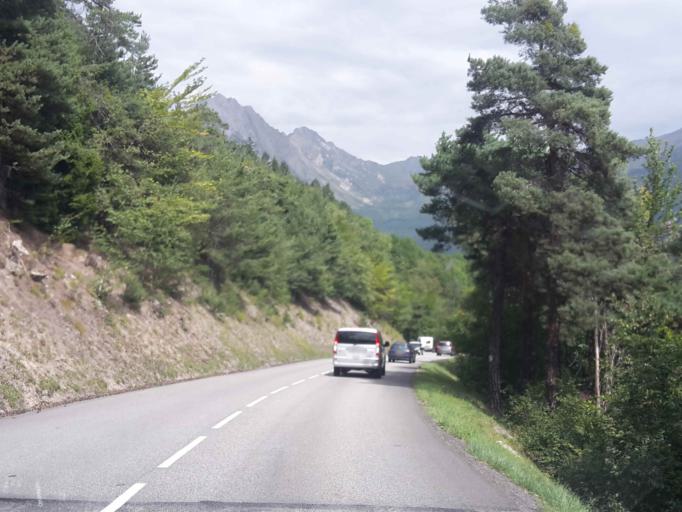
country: FR
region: Rhone-Alpes
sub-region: Departement de la Savoie
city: Saint-Michel-de-Maurienne
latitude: 45.2053
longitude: 6.4533
